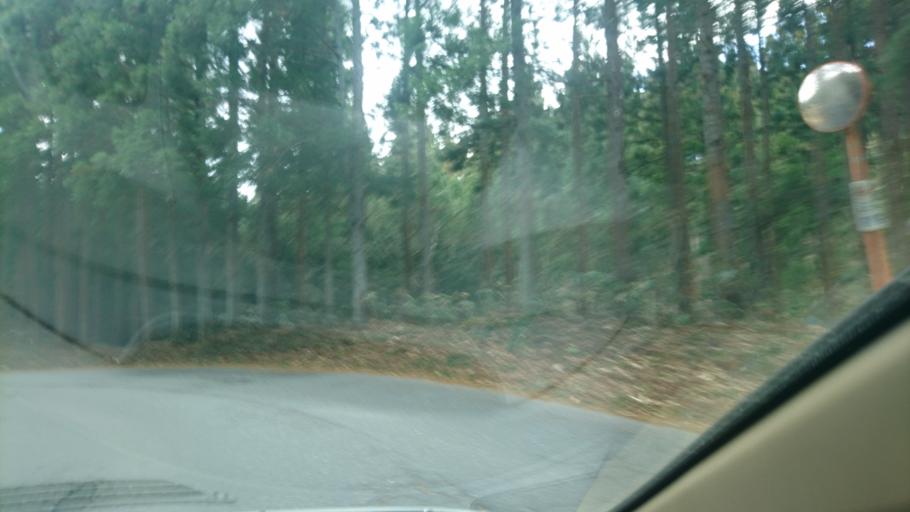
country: JP
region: Miyagi
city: Furukawa
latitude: 38.7242
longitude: 140.8310
